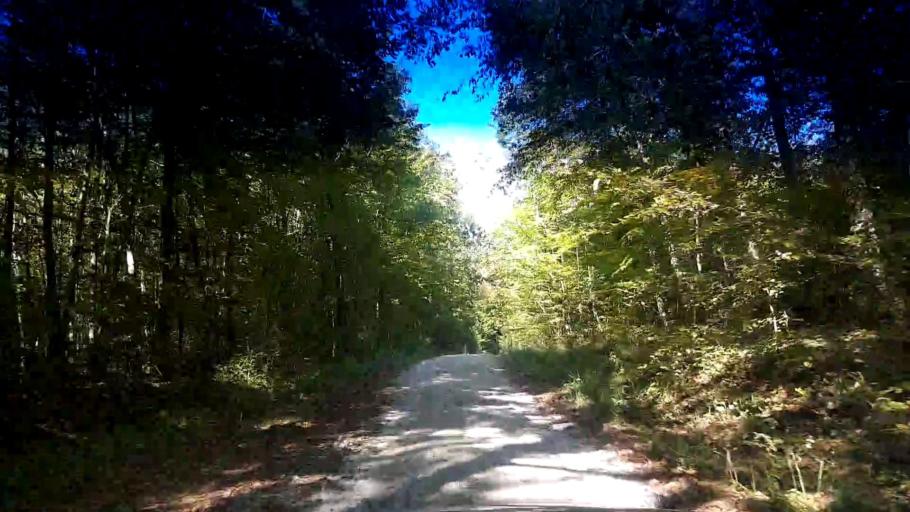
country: DE
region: Bavaria
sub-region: Upper Franconia
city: Litzendorf
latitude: 49.8935
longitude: 11.0203
